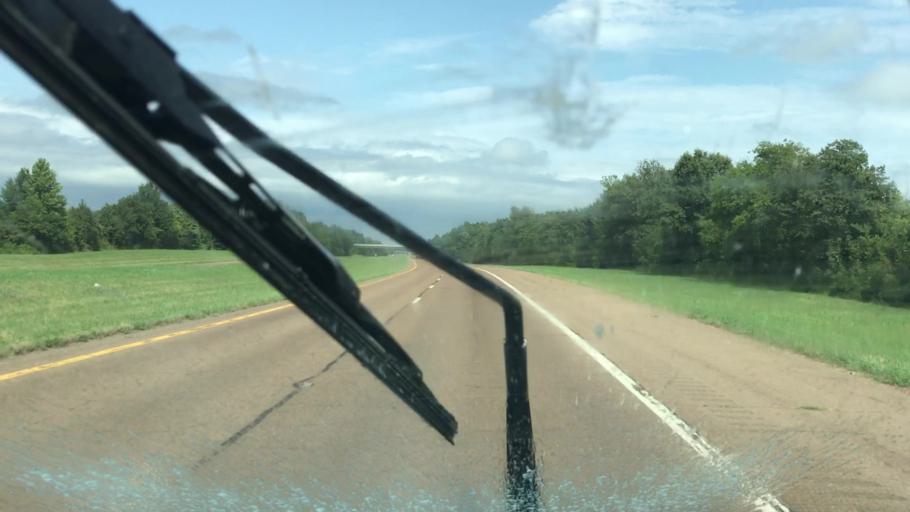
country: US
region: Tennessee
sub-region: Obion County
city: South Fulton
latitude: 36.4798
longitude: -88.9465
